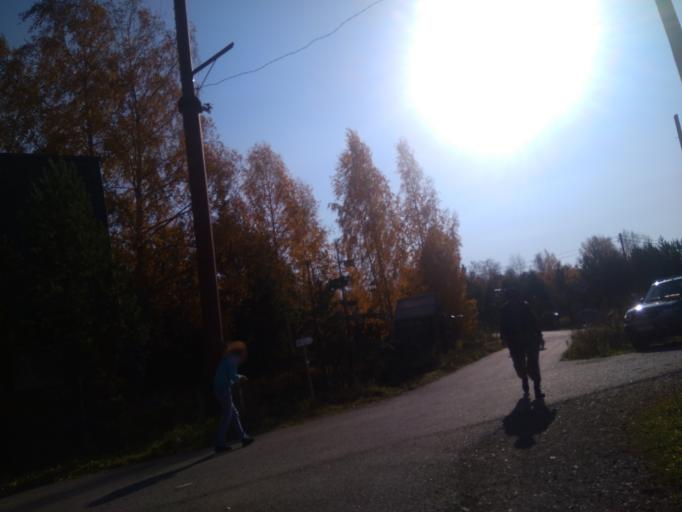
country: RU
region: Sverdlovsk
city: Mikhaylovsk
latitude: 56.5249
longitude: 59.2295
